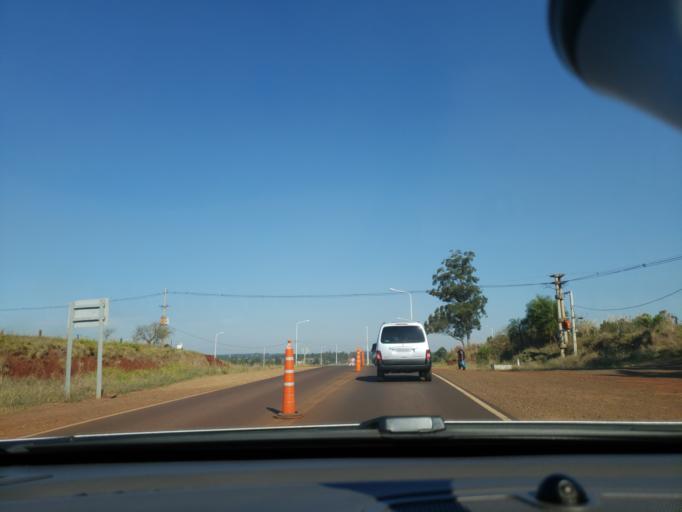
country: AR
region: Misiones
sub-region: Departamento de Capital
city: Posadas
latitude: -27.4629
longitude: -55.9707
